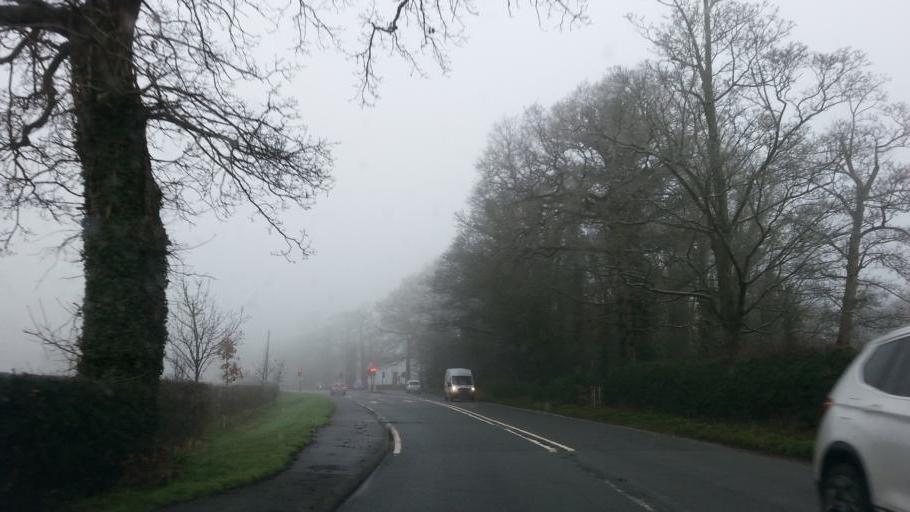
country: GB
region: England
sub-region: Cheshire East
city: Siddington
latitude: 53.2662
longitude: -2.2346
